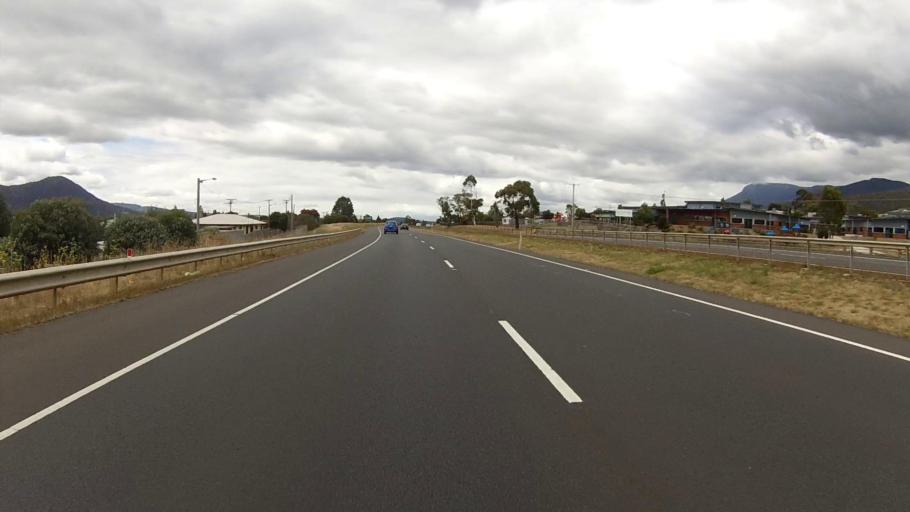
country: AU
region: Tasmania
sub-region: Glenorchy
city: Claremont
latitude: -42.7831
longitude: 147.2400
